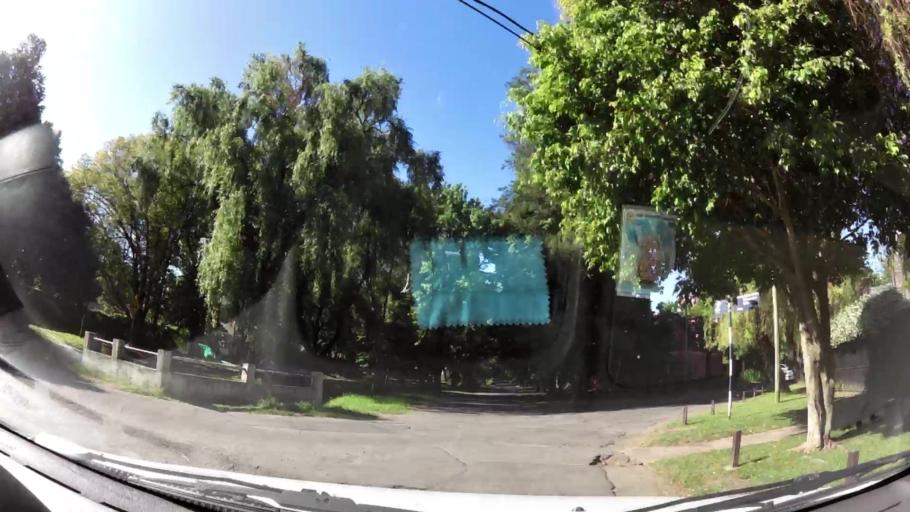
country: AR
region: Buenos Aires
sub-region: Partido de San Isidro
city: San Isidro
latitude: -34.4799
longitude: -58.5424
